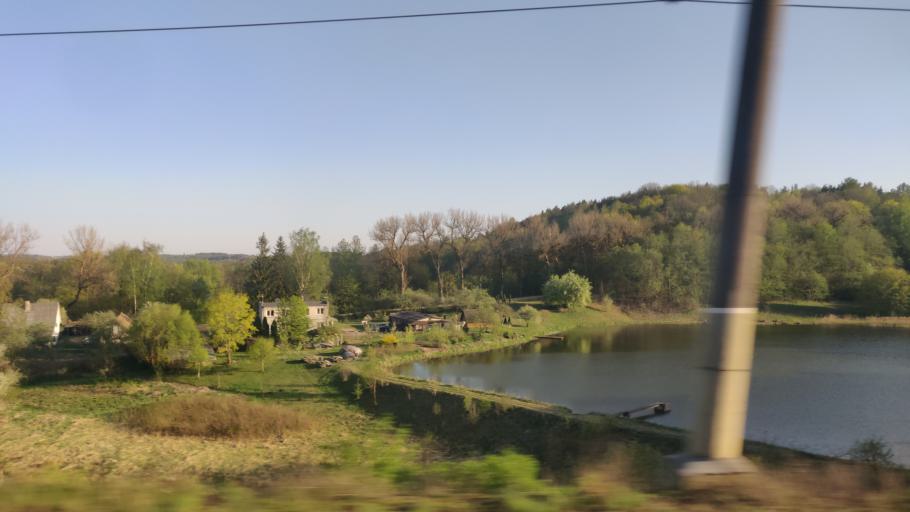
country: LT
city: Grigiskes
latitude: 54.6331
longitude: 25.1172
